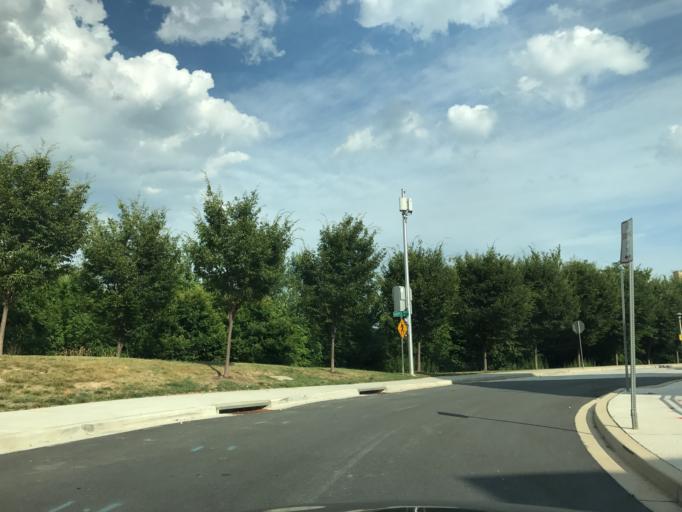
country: US
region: Maryland
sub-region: City of Baltimore
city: Baltimore
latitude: 39.2689
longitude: -76.5884
